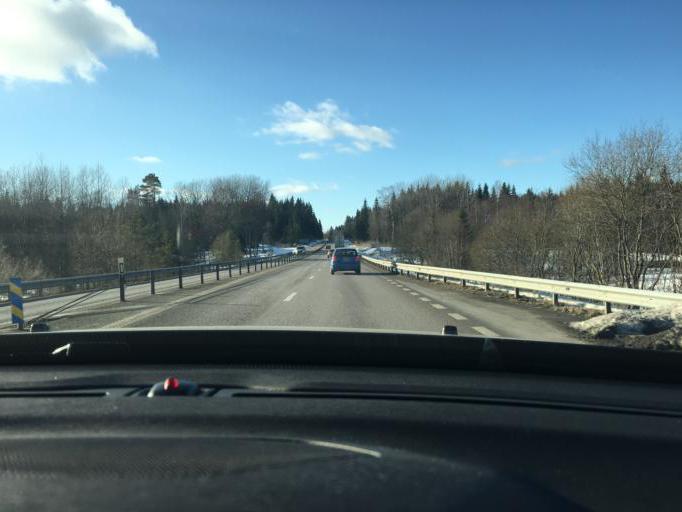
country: SE
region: Vaestra Goetaland
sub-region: Ulricehamns Kommun
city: Ulricehamn
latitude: 57.7973
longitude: 13.5368
